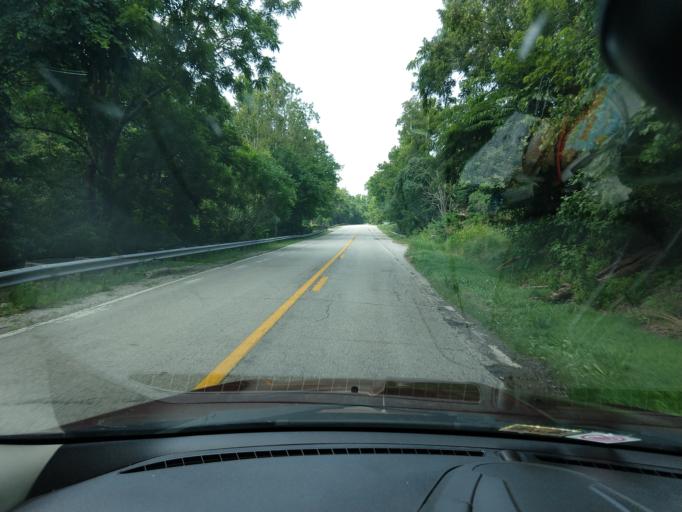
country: US
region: West Virginia
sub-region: Mason County
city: New Haven
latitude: 38.9234
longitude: -81.9133
